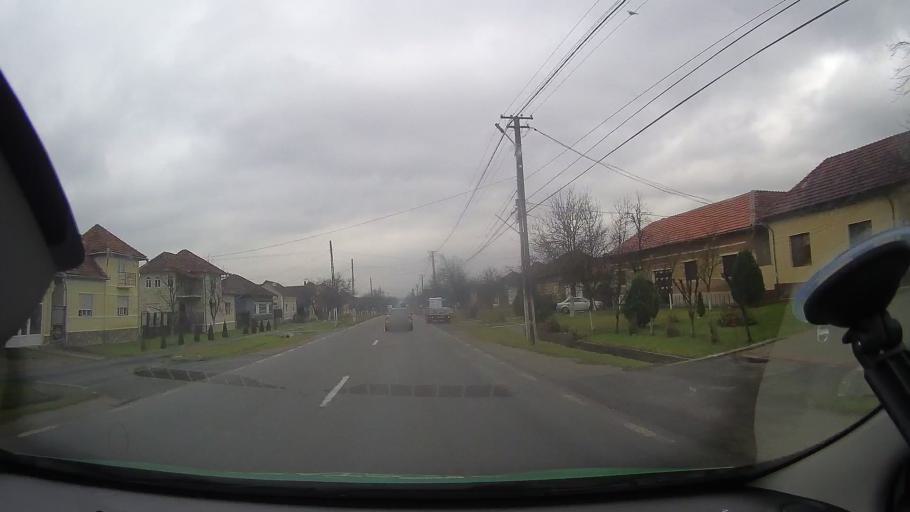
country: RO
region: Arad
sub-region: Comuna Almas
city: Almas
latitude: 46.2841
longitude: 22.2570
